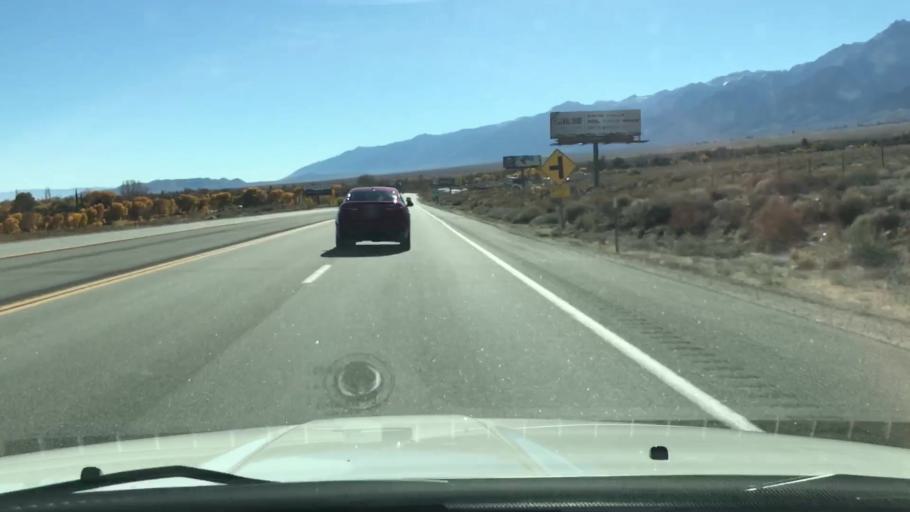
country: US
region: California
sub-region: Inyo County
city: Lone Pine
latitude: 36.8429
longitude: -118.2269
